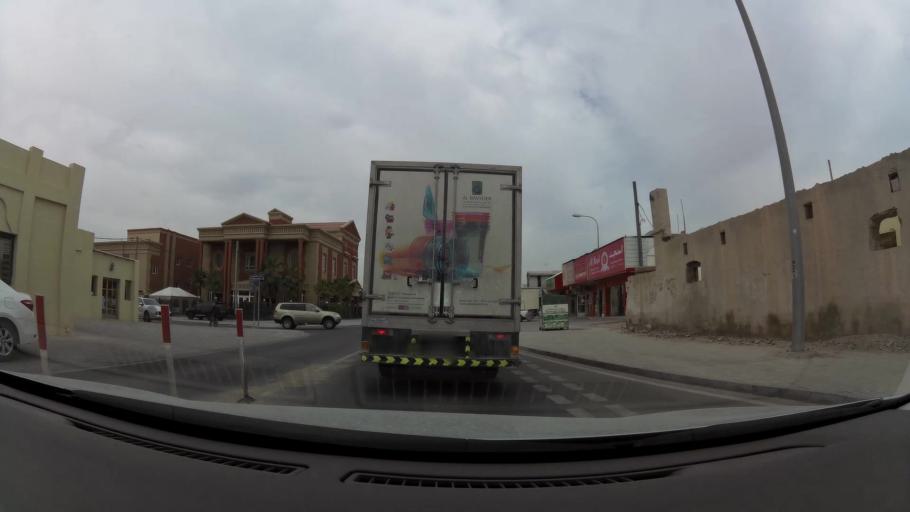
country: QA
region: Baladiyat ar Rayyan
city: Ar Rayyan
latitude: 25.2357
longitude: 51.4442
